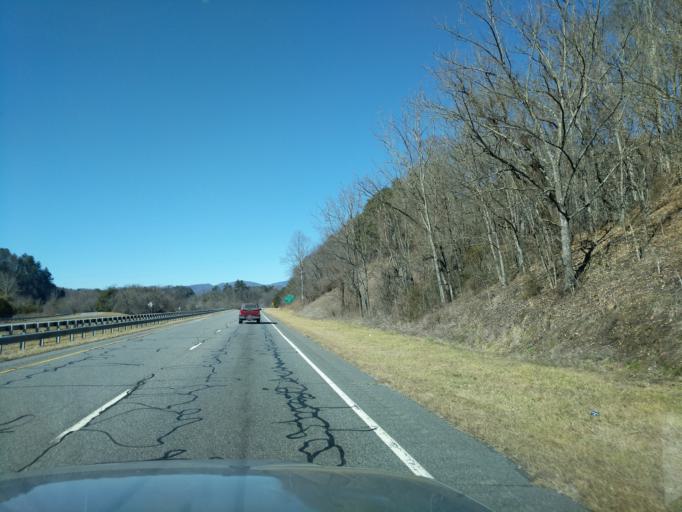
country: US
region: North Carolina
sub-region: Swain County
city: Cherokee
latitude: 35.4276
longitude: -83.3535
